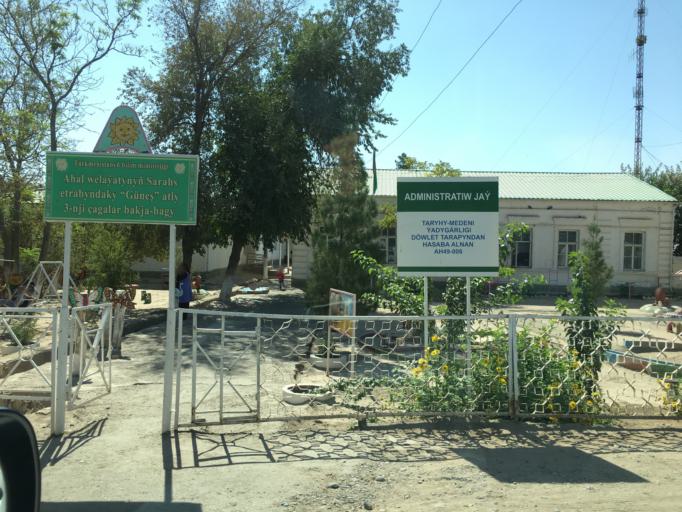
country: IR
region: Razavi Khorasan
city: Sarakhs
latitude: 36.5264
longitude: 61.2128
